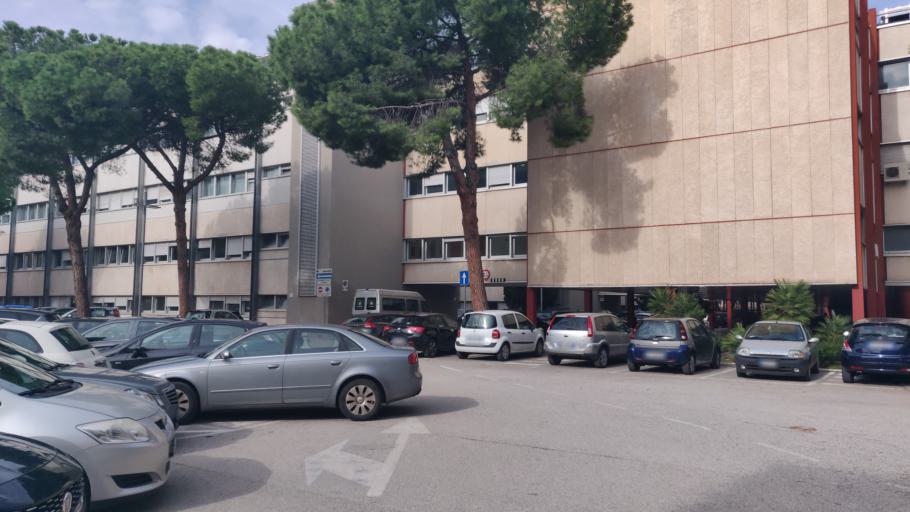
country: IT
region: Apulia
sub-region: Provincia di Bari
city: Bari
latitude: 41.1082
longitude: 16.8785
